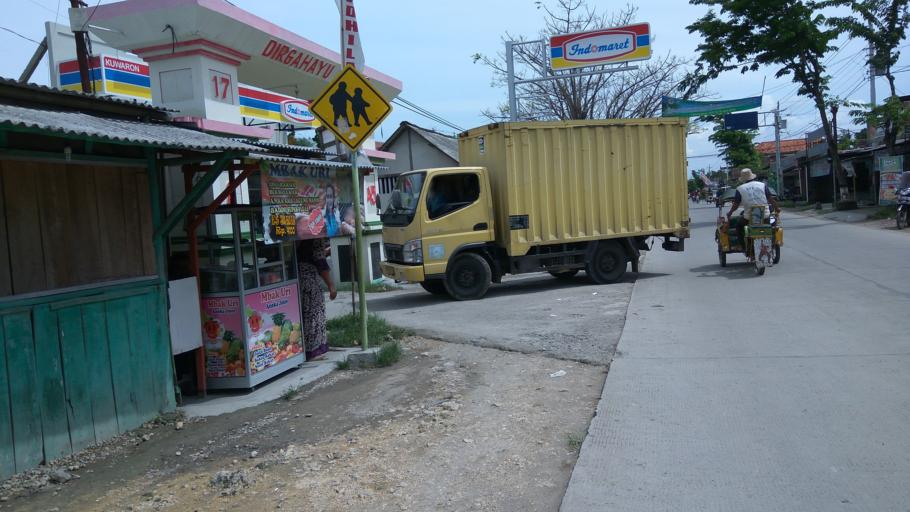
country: ID
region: Central Java
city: Mranggen
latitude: -7.0608
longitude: 110.6670
